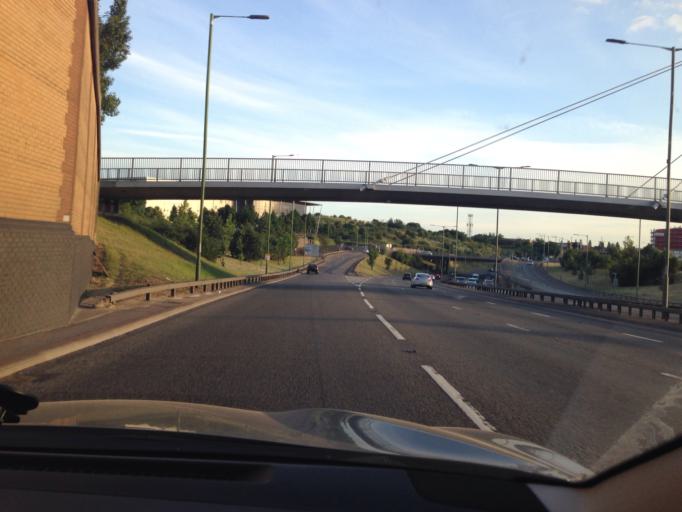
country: GB
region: England
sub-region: Greater London
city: Wembley
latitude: 51.5414
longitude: -0.2760
